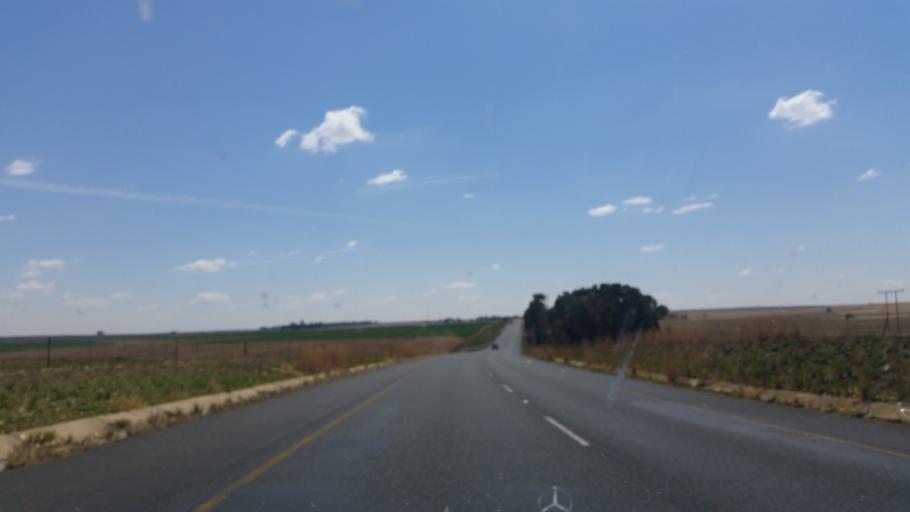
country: ZA
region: Orange Free State
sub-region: Thabo Mofutsanyana District Municipality
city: Bethlehem
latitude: -28.1017
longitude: 28.6587
